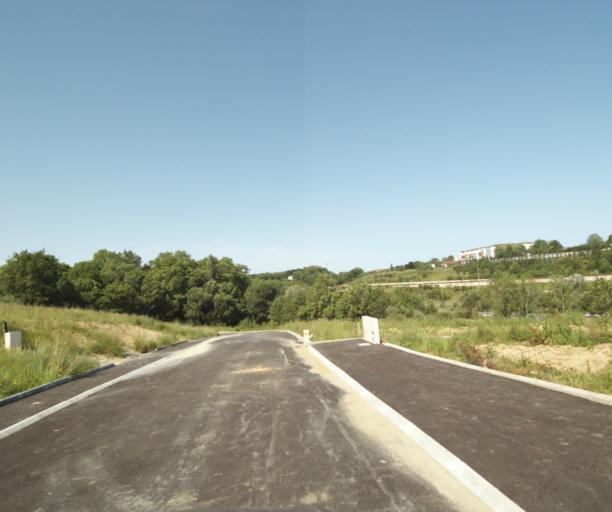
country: FR
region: Aquitaine
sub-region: Departement des Pyrenees-Atlantiques
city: Mouguerre
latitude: 43.4762
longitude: -1.4461
